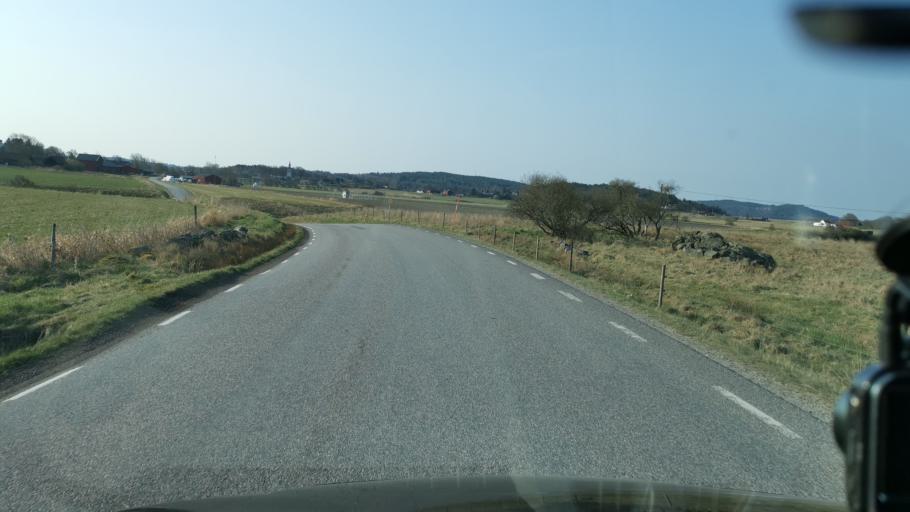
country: SE
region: Vaestra Goetaland
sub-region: Kungalvs Kommun
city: Kode
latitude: 57.9518
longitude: 11.8184
